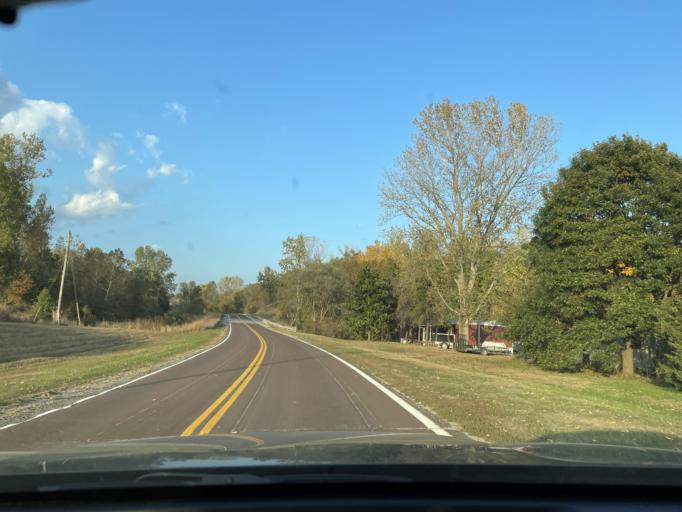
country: US
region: Missouri
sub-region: Andrew County
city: Savannah
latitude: 39.9060
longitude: -94.8806
